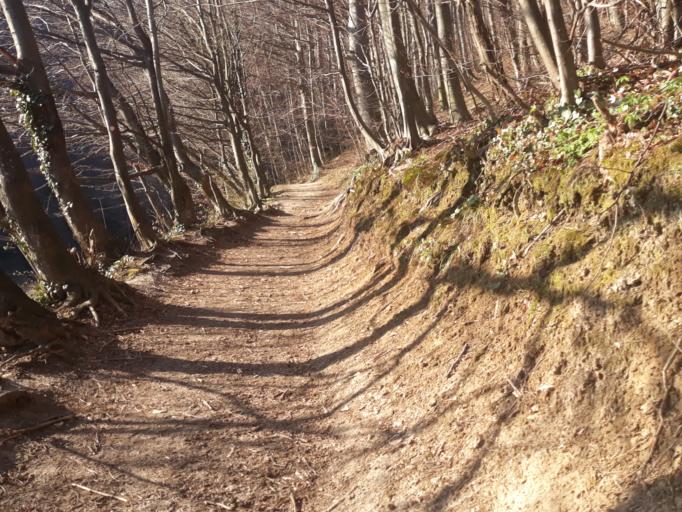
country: HR
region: Varazdinska
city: Ivanec
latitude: 46.1950
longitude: 16.1377
